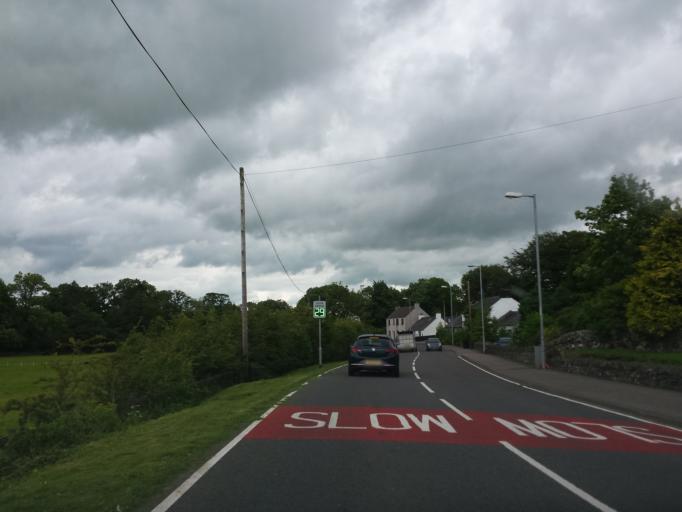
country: GB
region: Scotland
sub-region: Dumfries and Galloway
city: Dalbeattie
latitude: 55.0139
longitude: -3.8652
